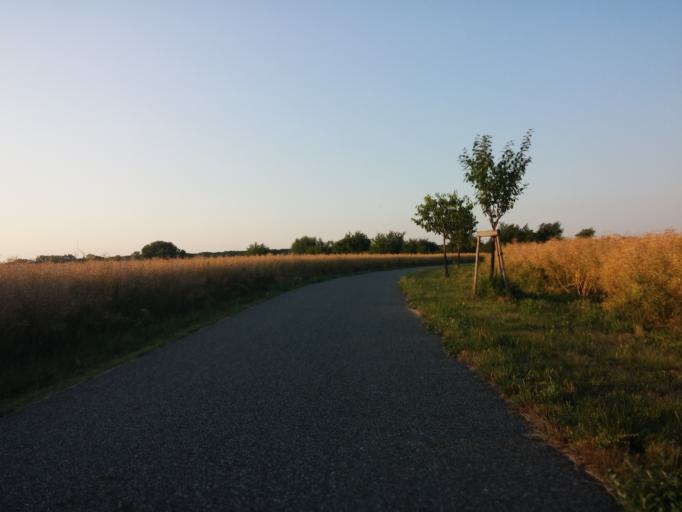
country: CZ
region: Central Bohemia
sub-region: Okres Nymburk
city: Podebrady
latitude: 50.1644
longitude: 15.1383
